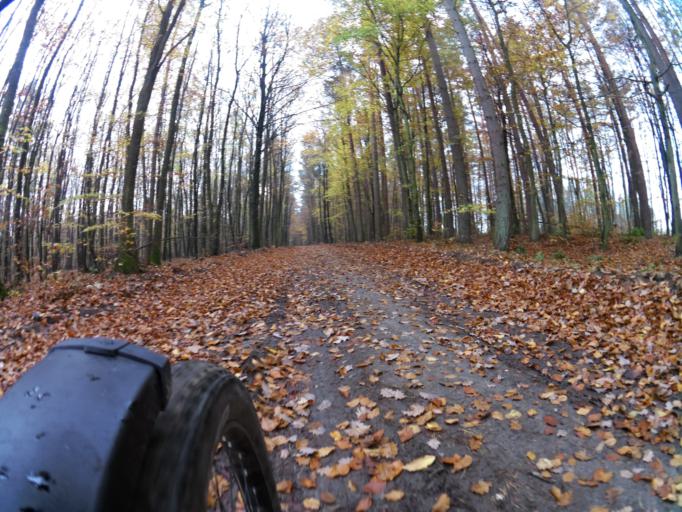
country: PL
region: Pomeranian Voivodeship
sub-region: Powiat pucki
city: Krokowa
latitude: 54.7746
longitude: 18.0915
